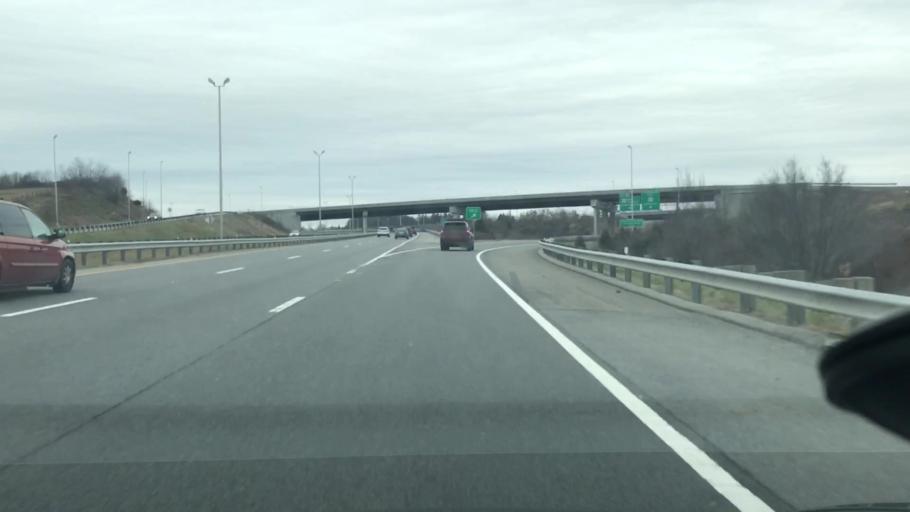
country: US
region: Virginia
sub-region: Montgomery County
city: Merrimac
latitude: 37.1868
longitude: -80.4016
